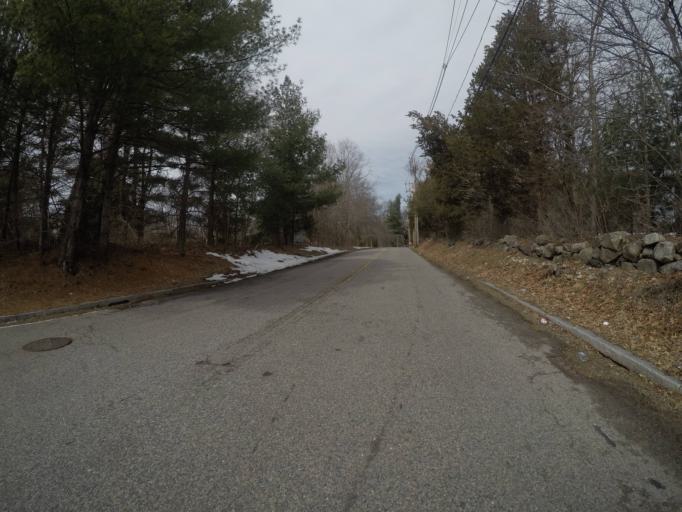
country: US
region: Massachusetts
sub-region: Bristol County
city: Easton
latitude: 42.0299
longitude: -71.1154
